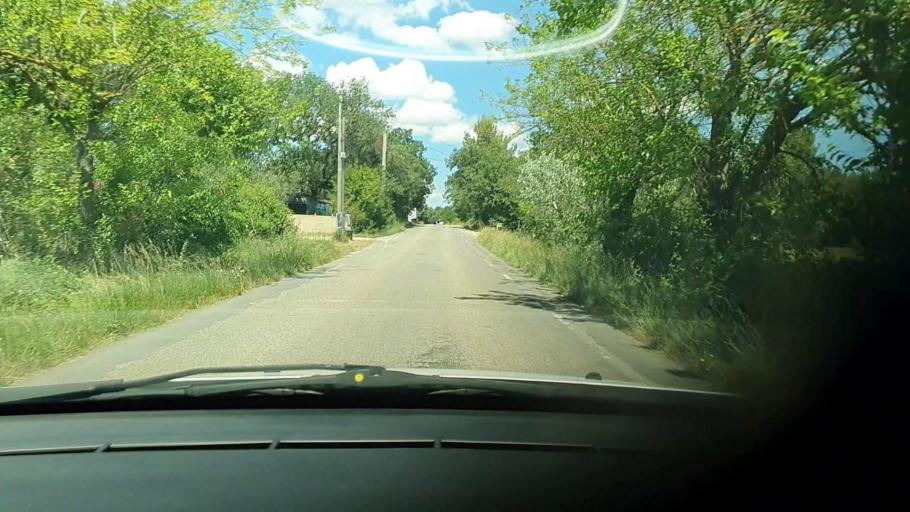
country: FR
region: Languedoc-Roussillon
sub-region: Departement du Gard
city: Blauzac
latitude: 43.9773
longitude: 4.3707
